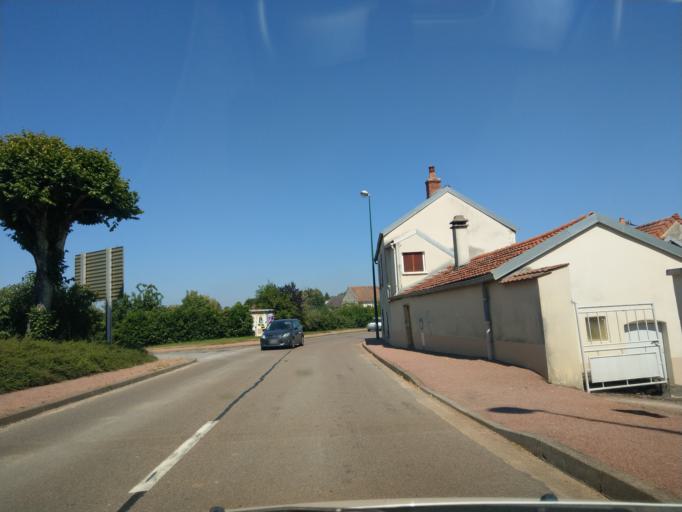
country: FR
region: Bourgogne
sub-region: Departement de la Cote-d'Or
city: Marcilly-sur-Tille
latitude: 47.5155
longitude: 5.1742
